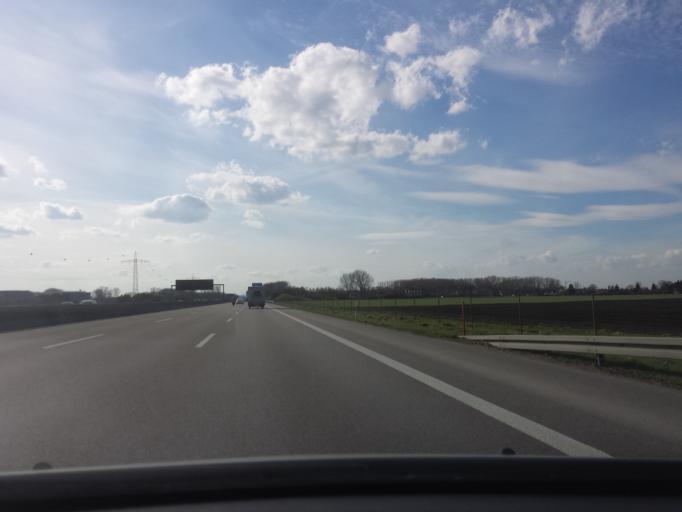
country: DE
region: Bavaria
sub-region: Swabia
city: Augsburg
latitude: 48.4056
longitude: 10.9458
